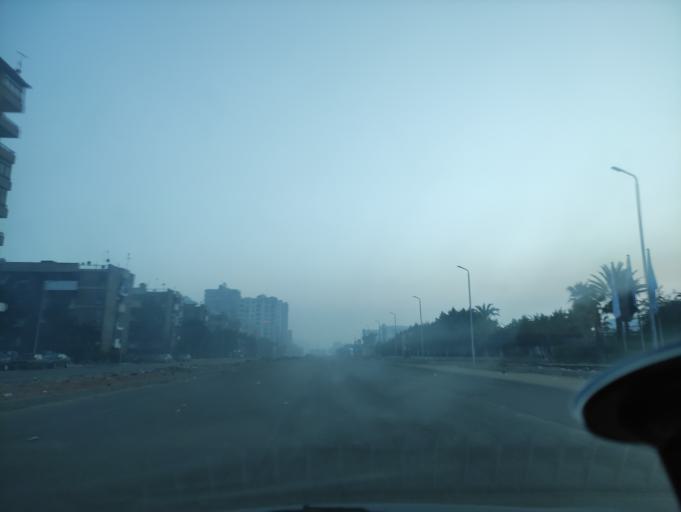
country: EG
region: Muhafazat al Qahirah
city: Cairo
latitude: 30.0456
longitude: 31.3482
